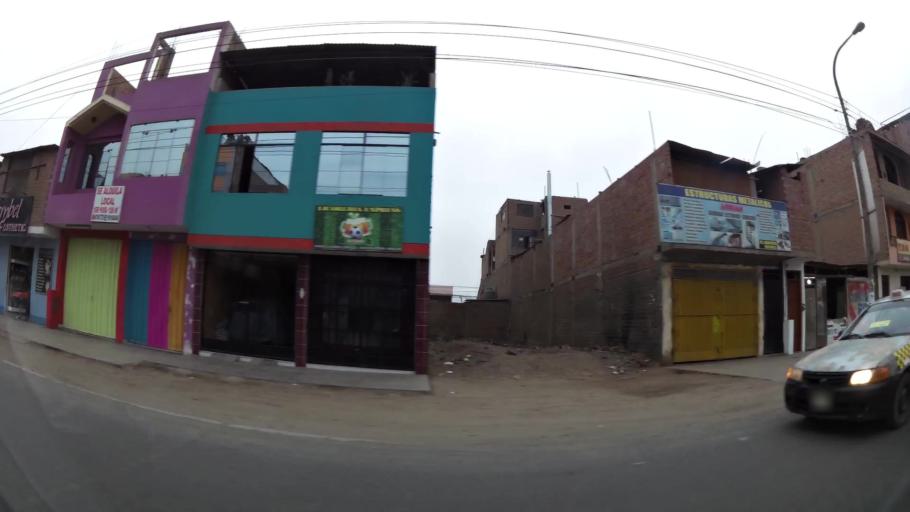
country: PE
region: Lima
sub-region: Lima
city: Urb. Santo Domingo
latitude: -11.8840
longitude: -77.0342
